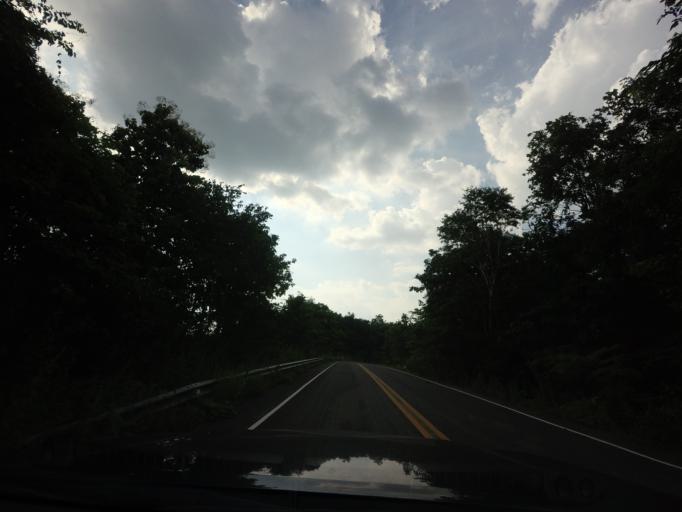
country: TH
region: Nan
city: Na Noi
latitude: 18.2892
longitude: 100.9043
